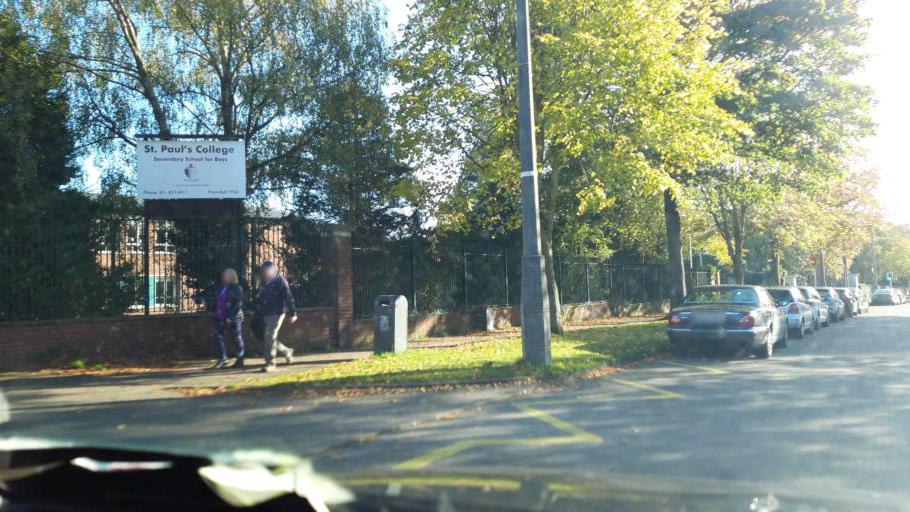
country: IE
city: Killester
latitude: 53.3730
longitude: -6.1941
